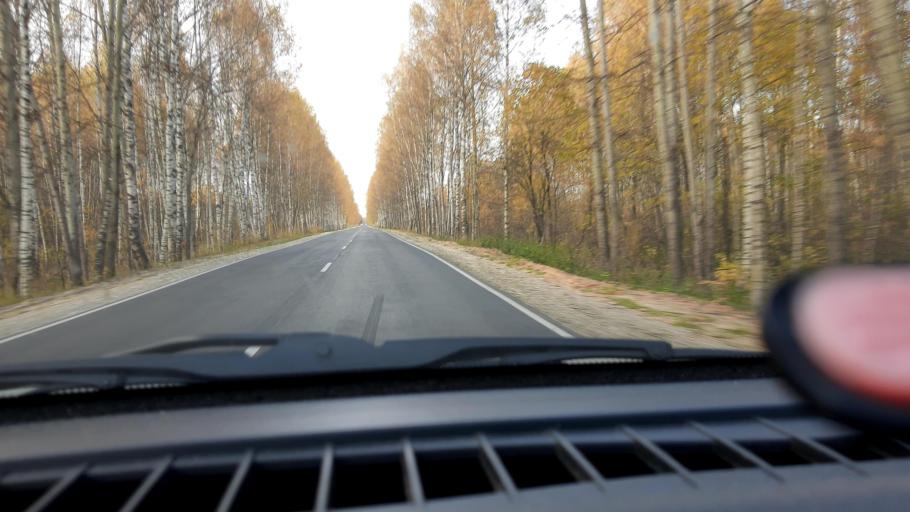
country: RU
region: Nizjnij Novgorod
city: Neklyudovo
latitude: 56.4891
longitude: 43.8624
